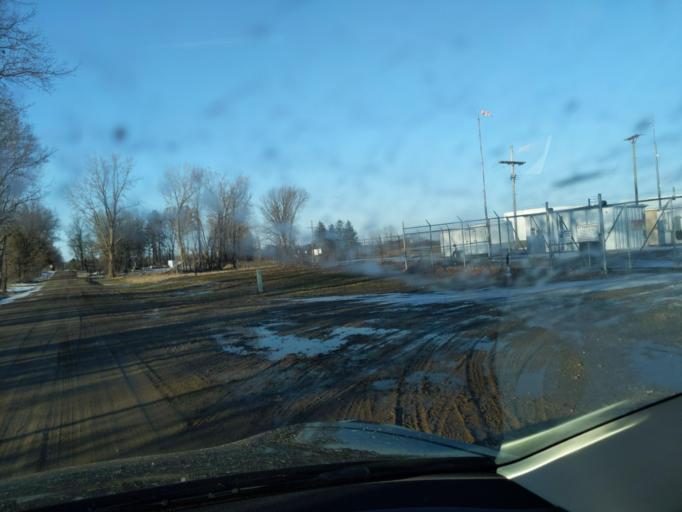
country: US
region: Michigan
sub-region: Ingham County
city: Stockbridge
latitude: 42.5122
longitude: -84.2440
